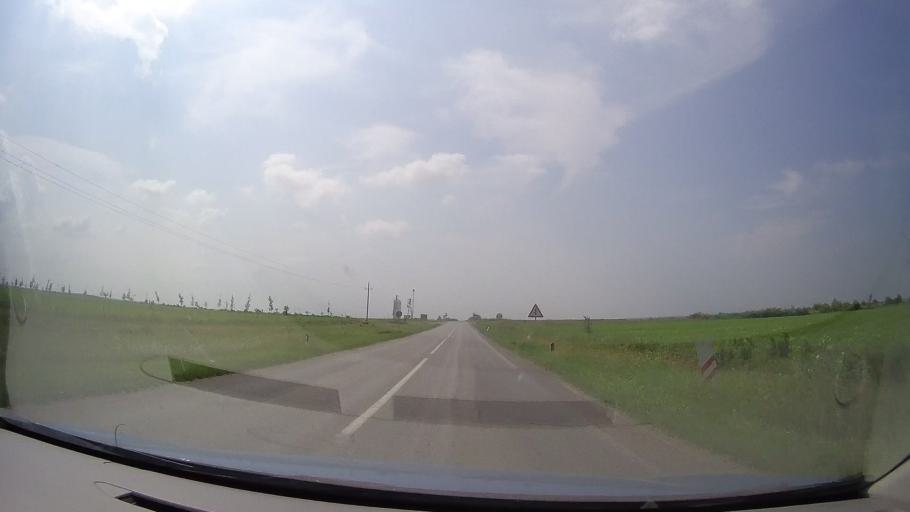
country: RS
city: Crepaja
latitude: 44.9919
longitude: 20.6424
